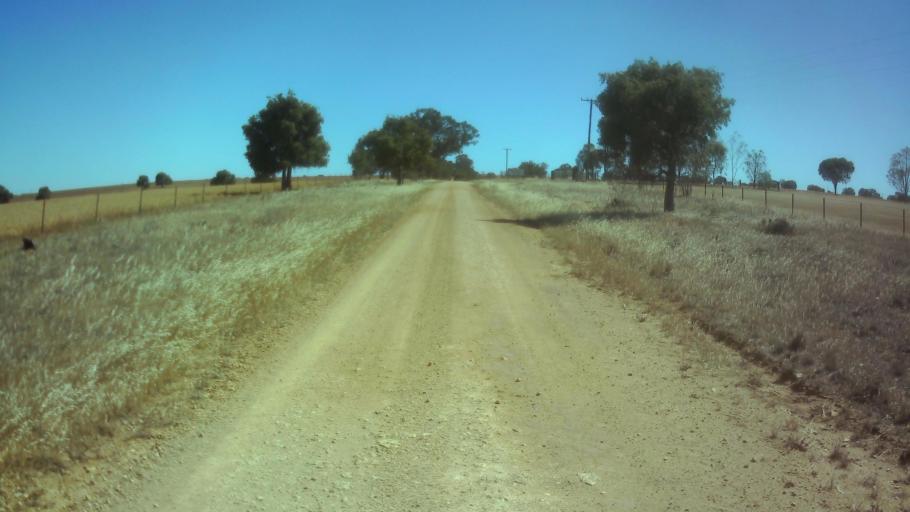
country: AU
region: New South Wales
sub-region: Weddin
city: Grenfell
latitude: -33.9835
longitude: 148.3414
